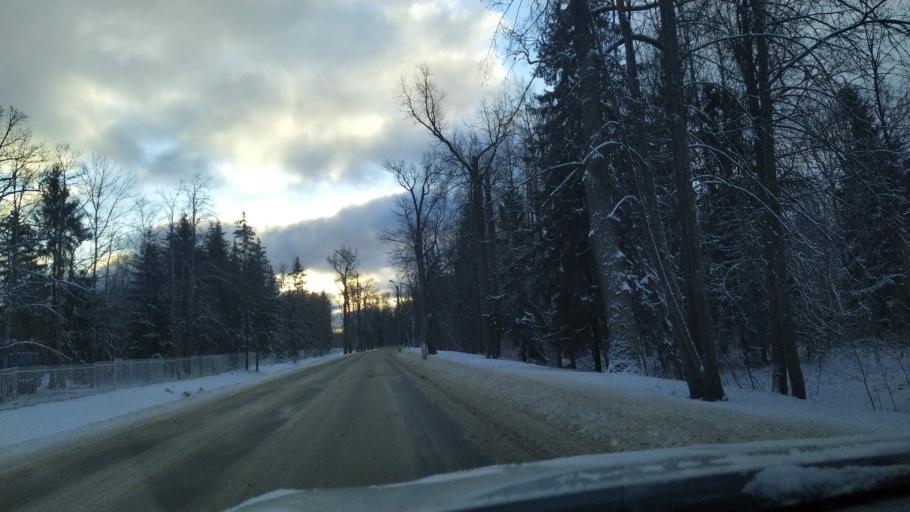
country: RU
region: St.-Petersburg
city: Pushkin
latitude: 59.7167
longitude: 30.3714
